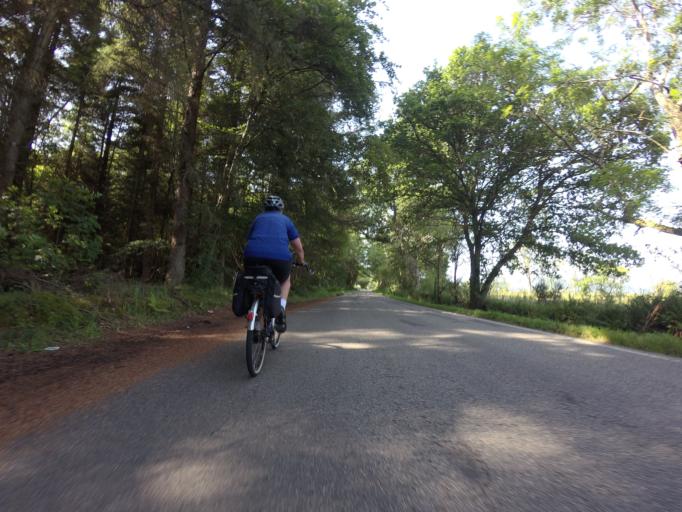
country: GB
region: Scotland
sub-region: Highland
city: Evanton
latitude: 57.6500
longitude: -4.3526
